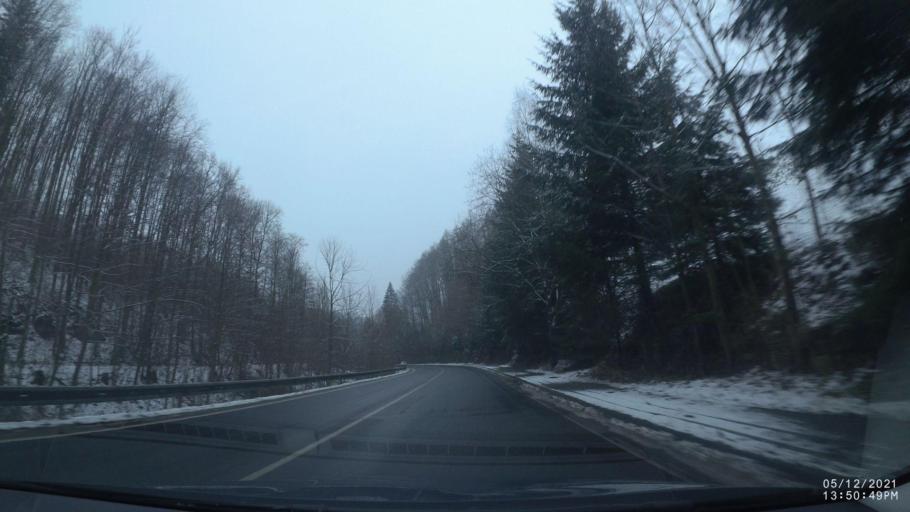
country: CZ
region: Kralovehradecky
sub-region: Okres Nachod
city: Police nad Metuji
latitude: 50.5333
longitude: 16.2264
